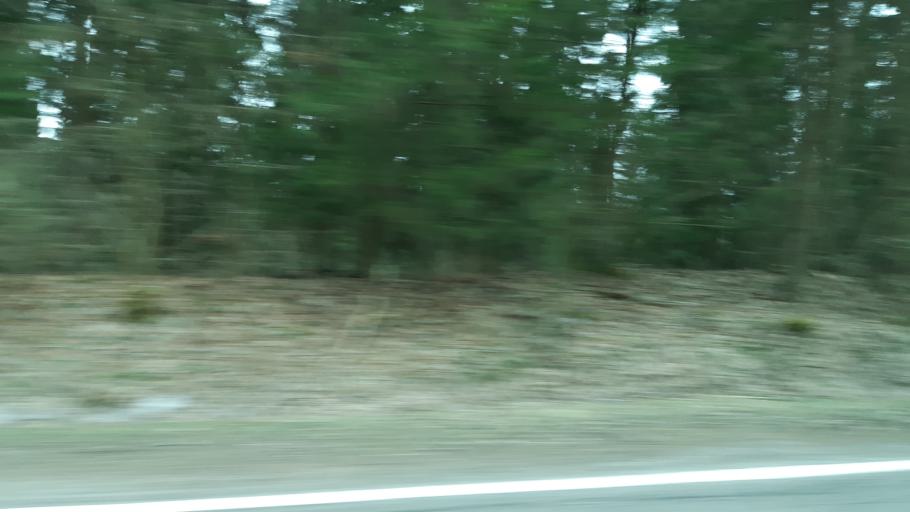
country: PL
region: Podlasie
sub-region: Suwalki
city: Suwalki
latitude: 54.3007
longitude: 22.9566
